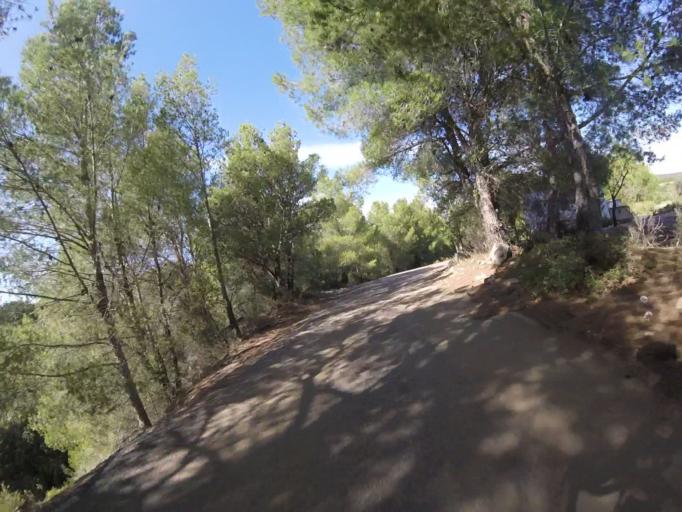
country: ES
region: Valencia
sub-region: Provincia de Castello
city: Sarratella
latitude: 40.2776
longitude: 0.0609
